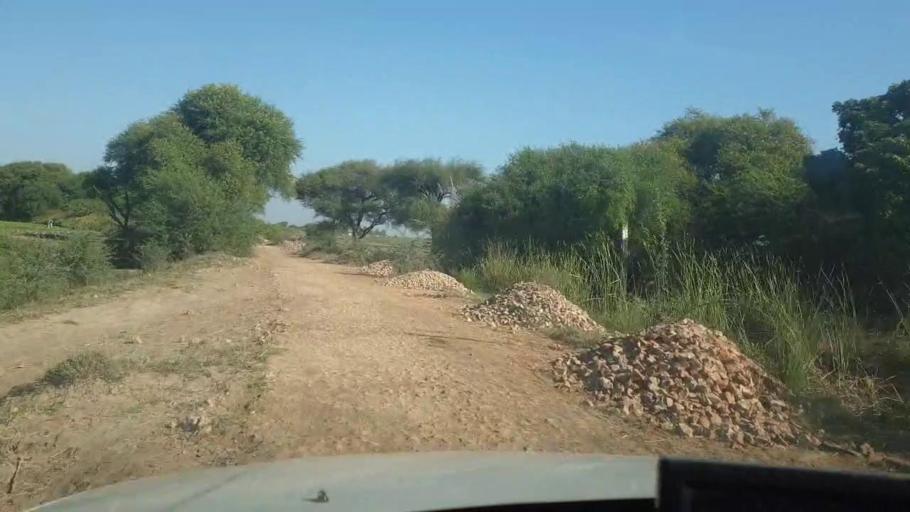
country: PK
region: Sindh
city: Mirpur Sakro
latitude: 24.4996
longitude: 67.6245
